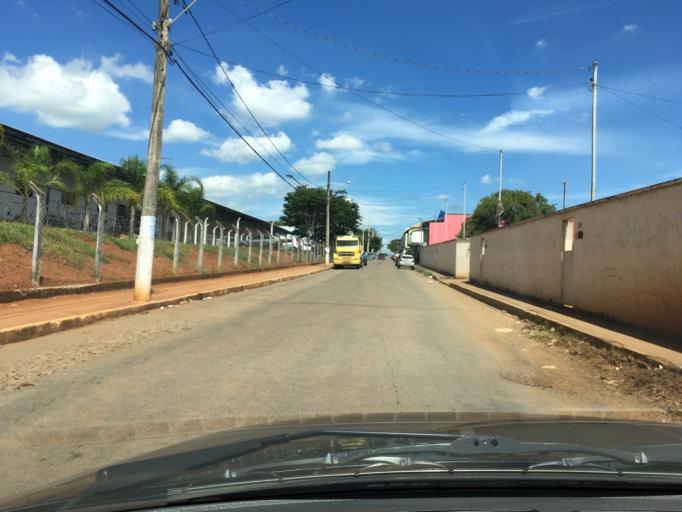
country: BR
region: Minas Gerais
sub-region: Mateus Leme
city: Mateus Leme
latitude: -19.9955
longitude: -44.4345
